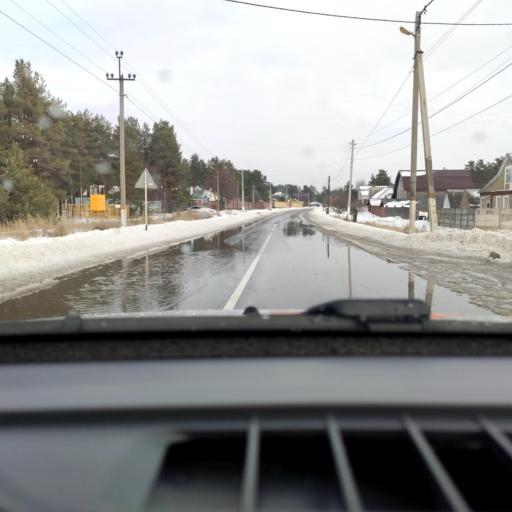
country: RU
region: Voronezj
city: Podgornoye
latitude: 51.7764
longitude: 39.1282
